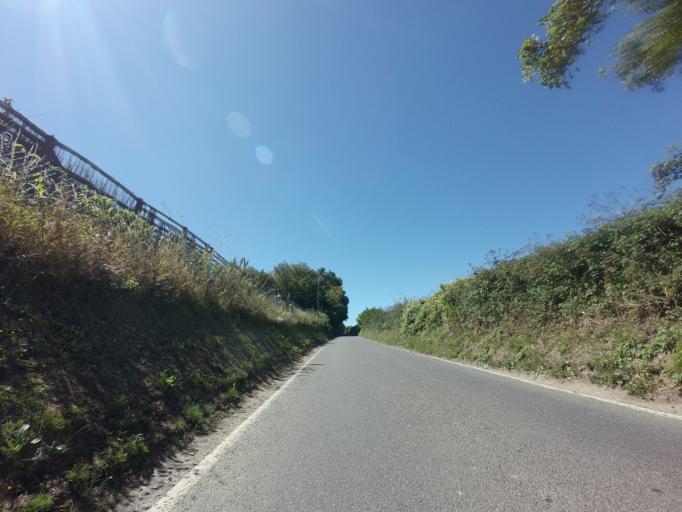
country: GB
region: England
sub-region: Kent
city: Eastry
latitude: 51.2475
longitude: 1.3025
